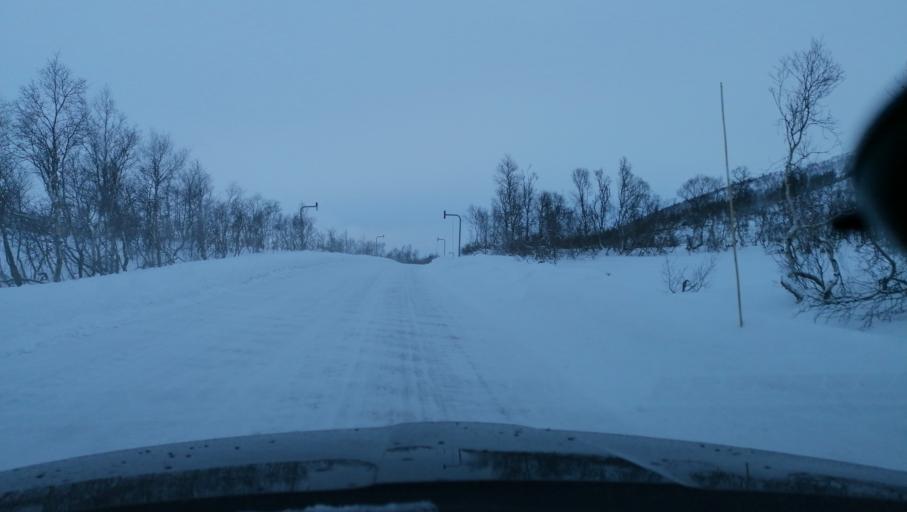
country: NO
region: Aust-Agder
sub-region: Bykle
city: Hovden
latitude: 59.6330
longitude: 7.4536
